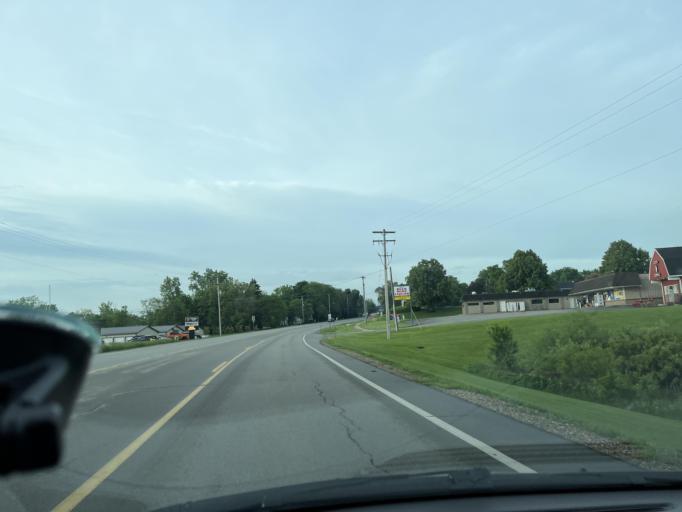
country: US
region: Michigan
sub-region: Barry County
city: Middleville
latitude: 42.7176
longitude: -85.4706
